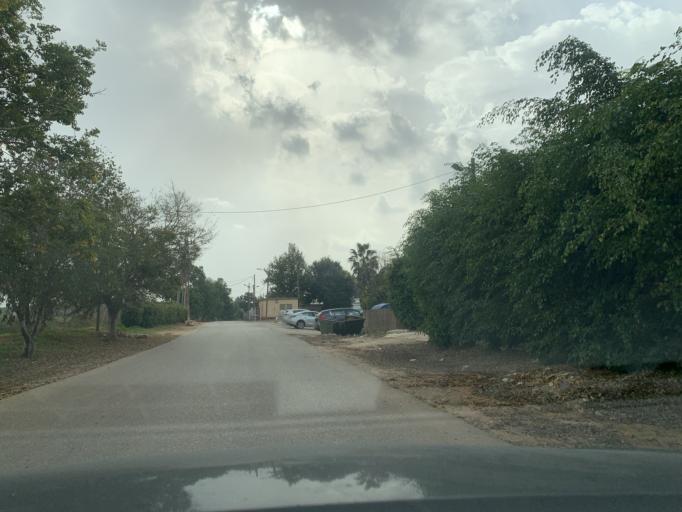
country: IL
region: Central District
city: Tirah
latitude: 32.2163
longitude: 34.9414
